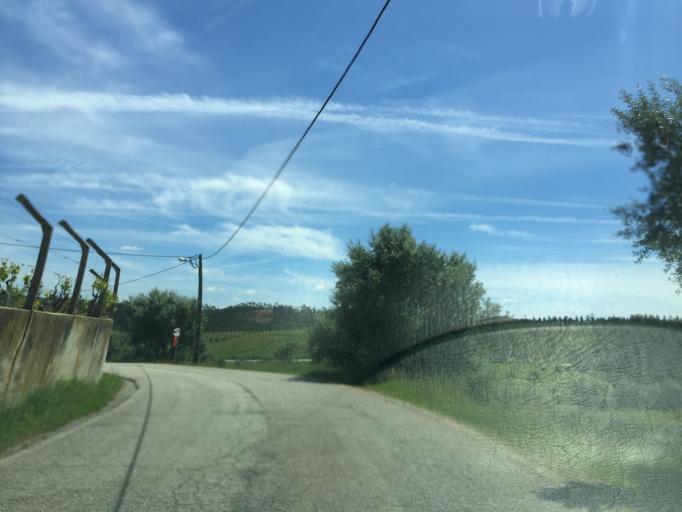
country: PT
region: Coimbra
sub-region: Soure
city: Soure
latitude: 40.0517
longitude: -8.6732
